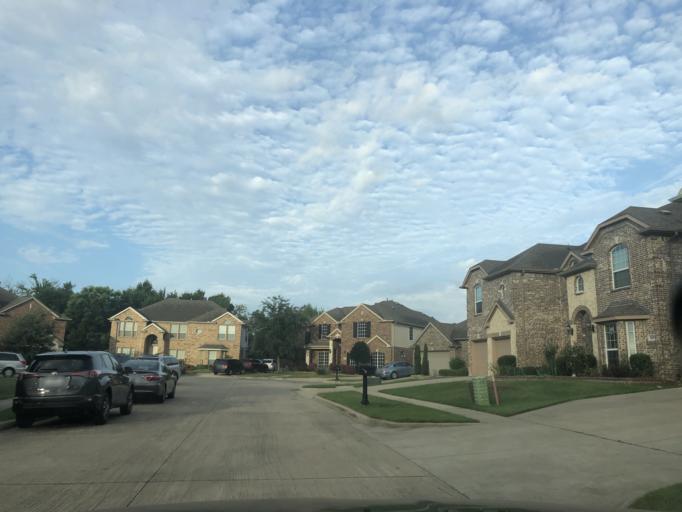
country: US
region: Texas
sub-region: Dallas County
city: Rowlett
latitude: 32.8500
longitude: -96.5896
